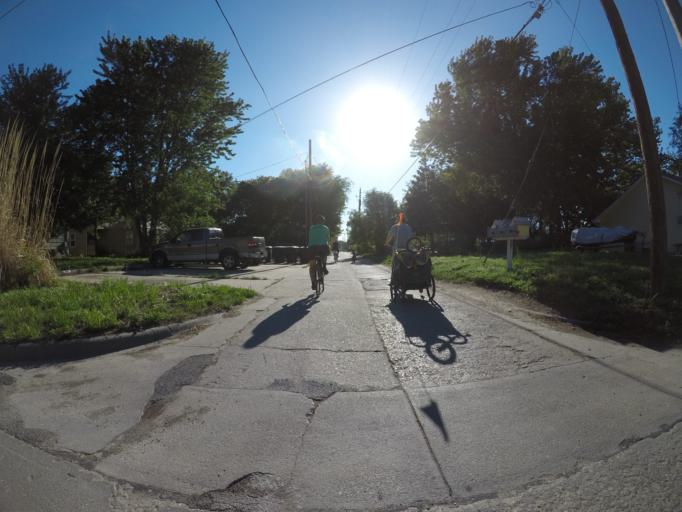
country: US
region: Kansas
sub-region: Riley County
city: Manhattan
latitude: 39.1727
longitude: -96.5702
